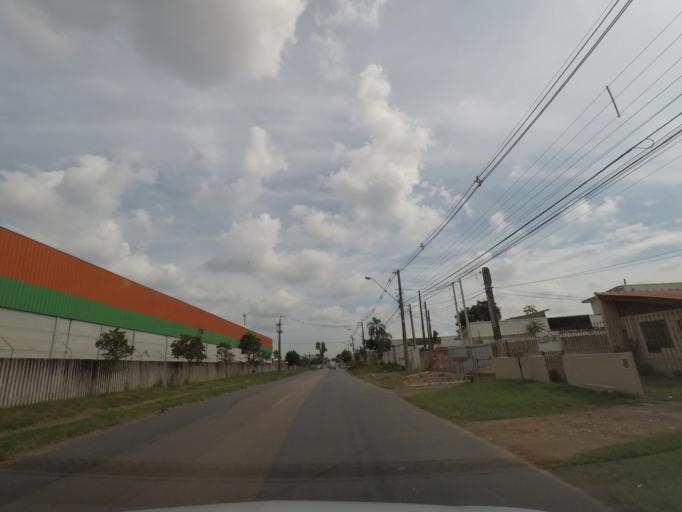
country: BR
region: Parana
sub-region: Sao Jose Dos Pinhais
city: Sao Jose dos Pinhais
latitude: -25.5006
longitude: -49.2134
